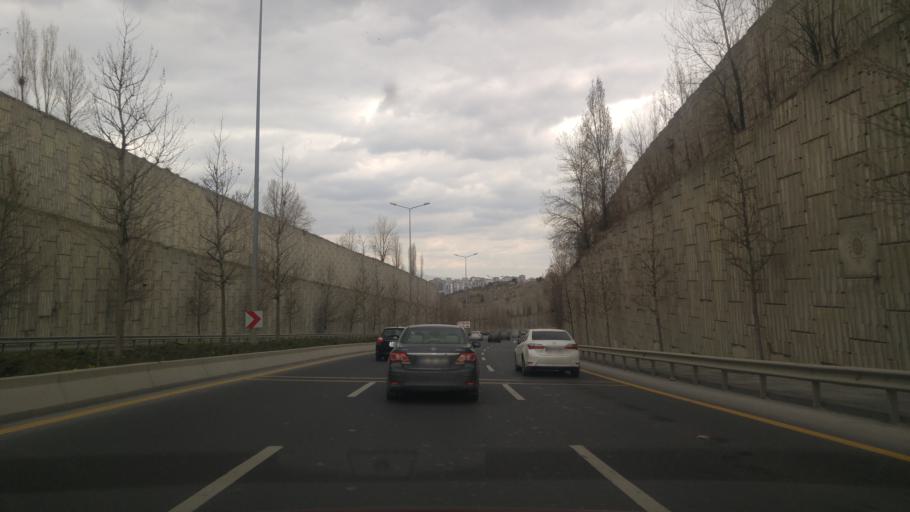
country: TR
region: Ankara
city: Cankaya
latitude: 39.8865
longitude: 32.8917
